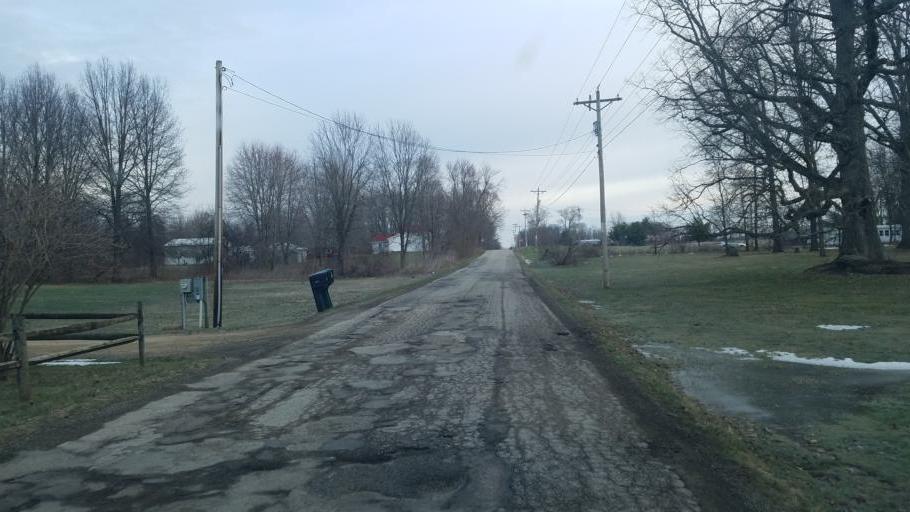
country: US
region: Ohio
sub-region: Morrow County
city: Mount Gilead
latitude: 40.4743
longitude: -82.7821
